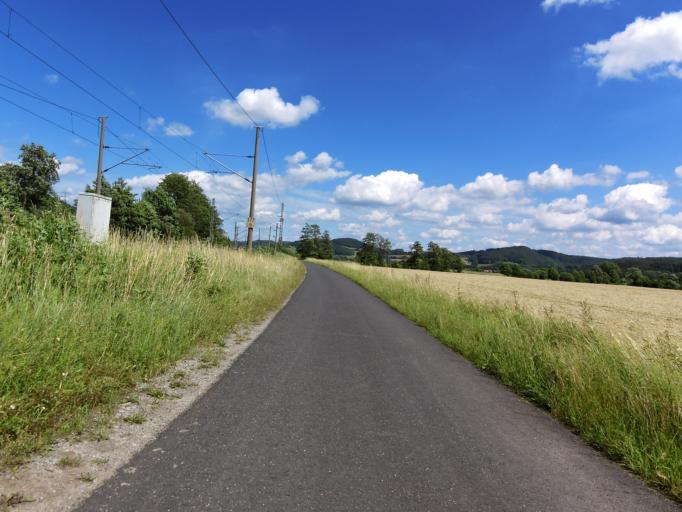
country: DE
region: Hesse
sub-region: Regierungsbezirk Kassel
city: Herleshausen
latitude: 51.0018
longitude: 10.1818
